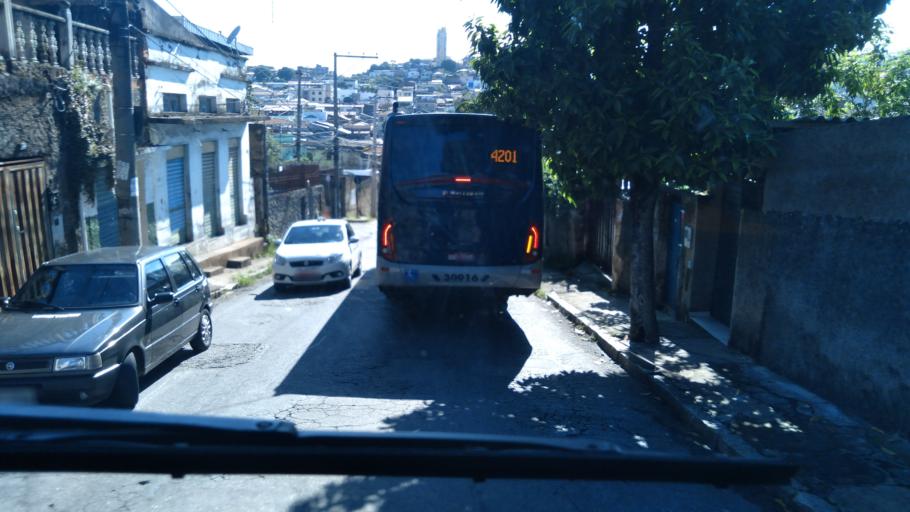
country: BR
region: Minas Gerais
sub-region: Belo Horizonte
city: Belo Horizonte
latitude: -19.9049
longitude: -43.9576
